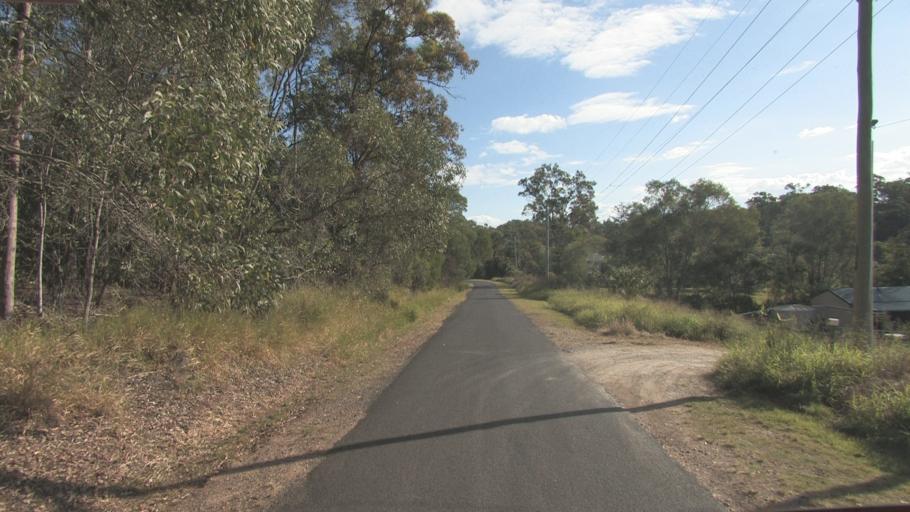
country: AU
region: Queensland
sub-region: Logan
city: Windaroo
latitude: -27.7405
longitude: 153.1646
